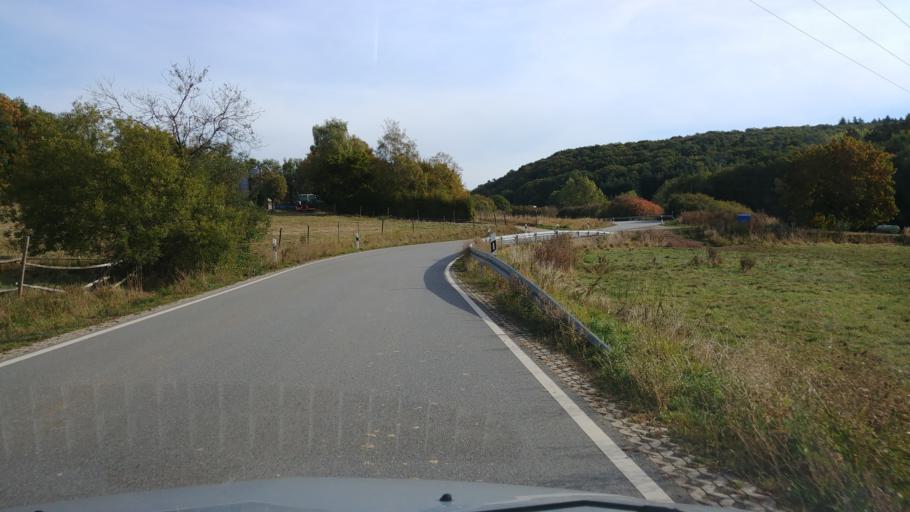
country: DE
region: Rheinland-Pfalz
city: Reckenroth
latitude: 50.2197
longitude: 8.0062
